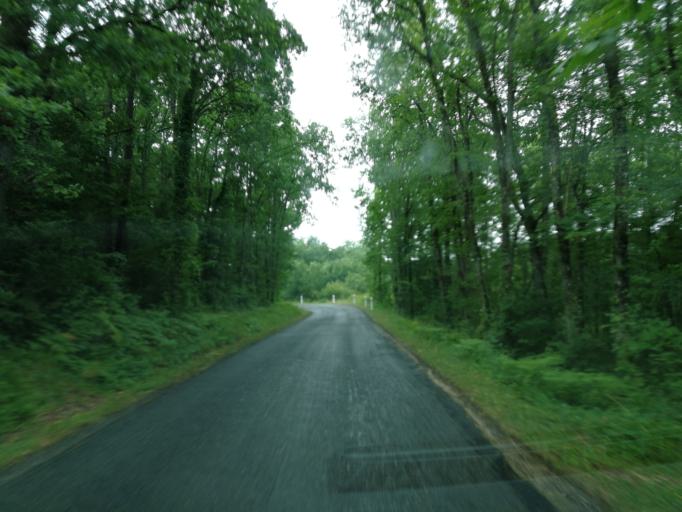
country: FR
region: Midi-Pyrenees
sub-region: Departement du Lot
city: Prayssac
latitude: 44.5366
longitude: 1.0871
